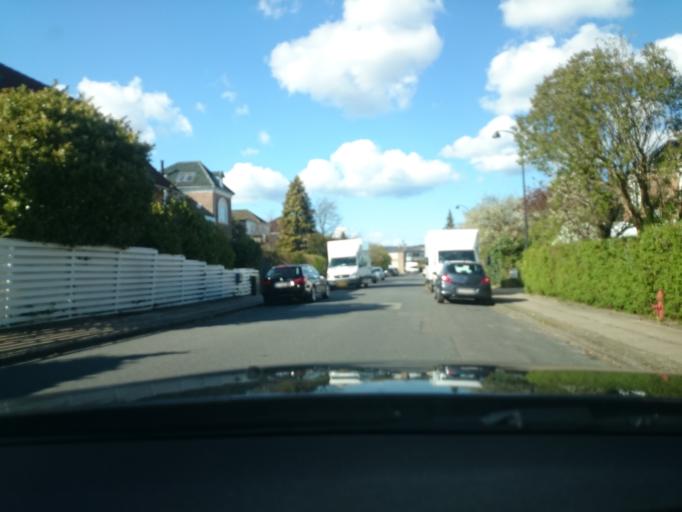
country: DK
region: Capital Region
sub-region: Gentofte Kommune
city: Charlottenlund
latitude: 55.7637
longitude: 12.5832
